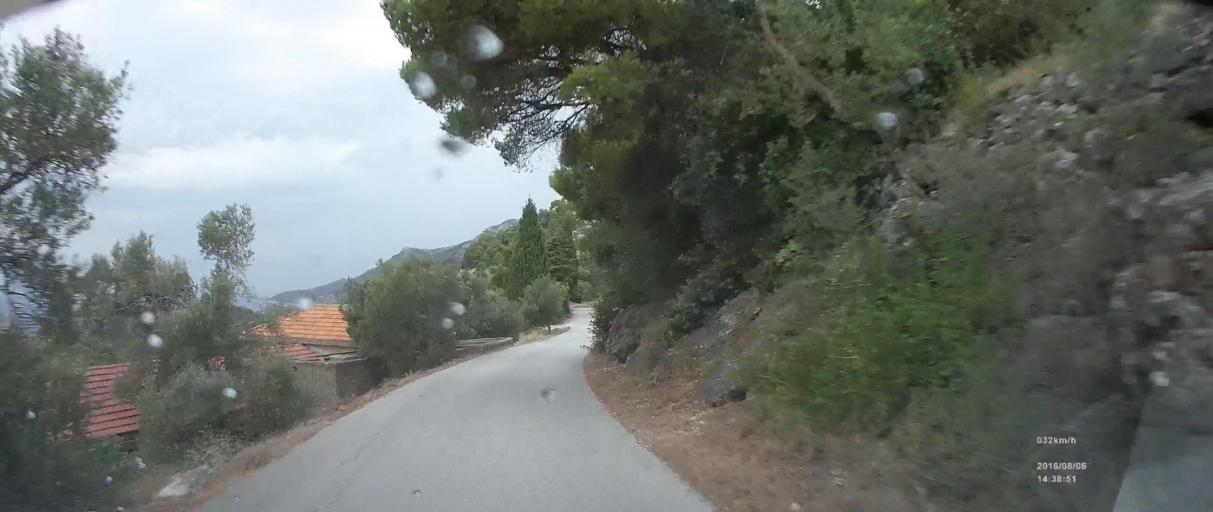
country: HR
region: Dubrovacko-Neretvanska
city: Ston
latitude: 42.7157
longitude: 17.6665
